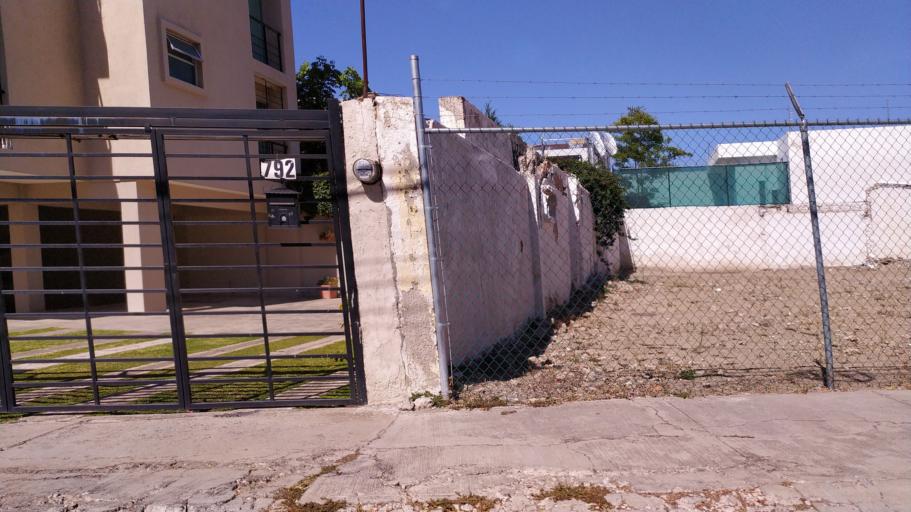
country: MX
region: Jalisco
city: Guadalajara
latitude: 20.6911
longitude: -103.3914
